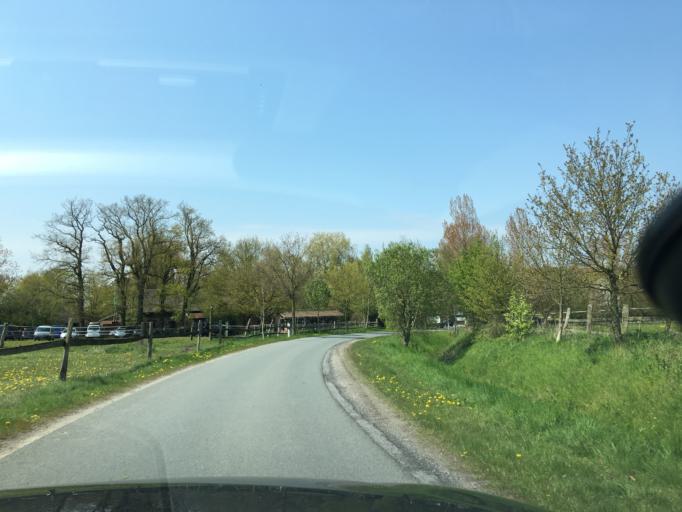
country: DE
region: North Rhine-Westphalia
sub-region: Regierungsbezirk Munster
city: Senden
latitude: 51.8233
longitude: 7.4655
